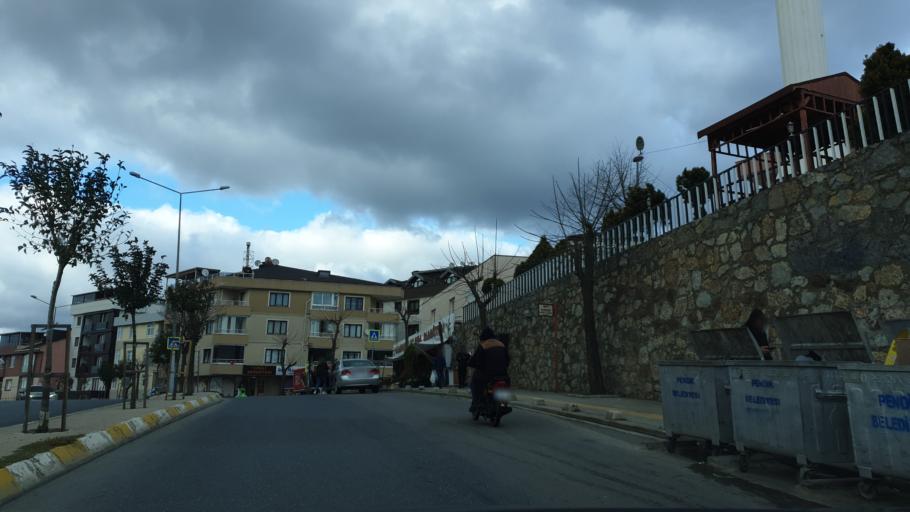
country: TR
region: Istanbul
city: Pendik
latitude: 40.9042
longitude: 29.2470
